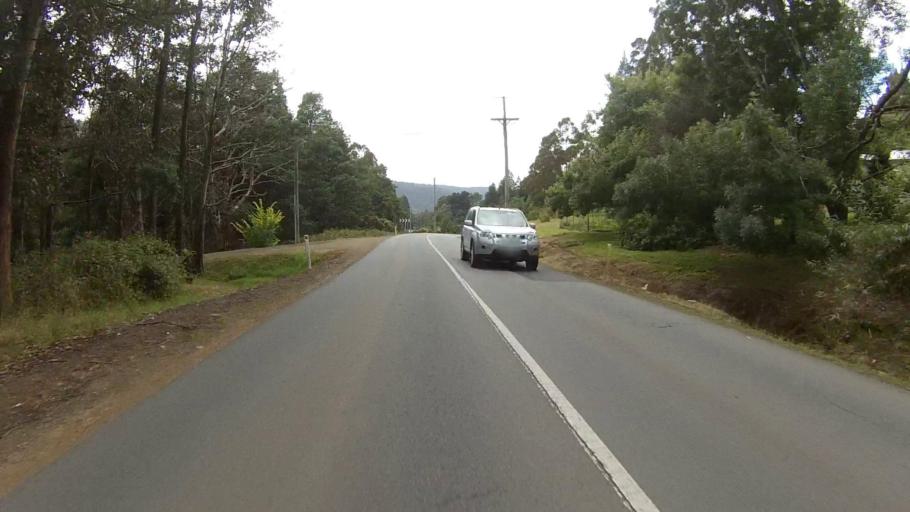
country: AU
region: Tasmania
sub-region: Kingborough
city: Kettering
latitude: -43.1159
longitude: 147.1904
